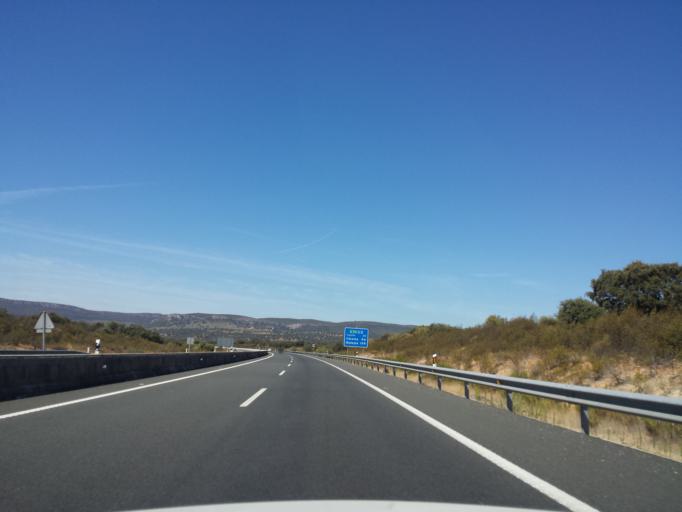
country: ES
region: Extremadura
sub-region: Provincia de Caceres
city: Almaraz
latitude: 39.7893
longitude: -5.7096
